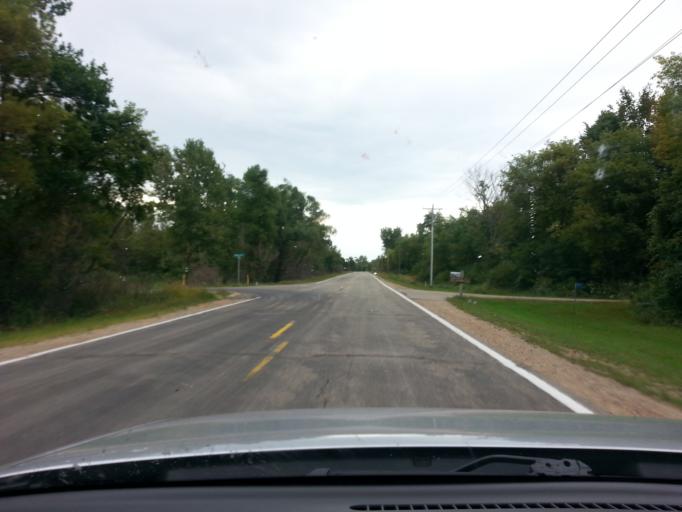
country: US
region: Minnesota
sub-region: Dakota County
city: Lakeville
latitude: 44.6636
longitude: -93.3374
